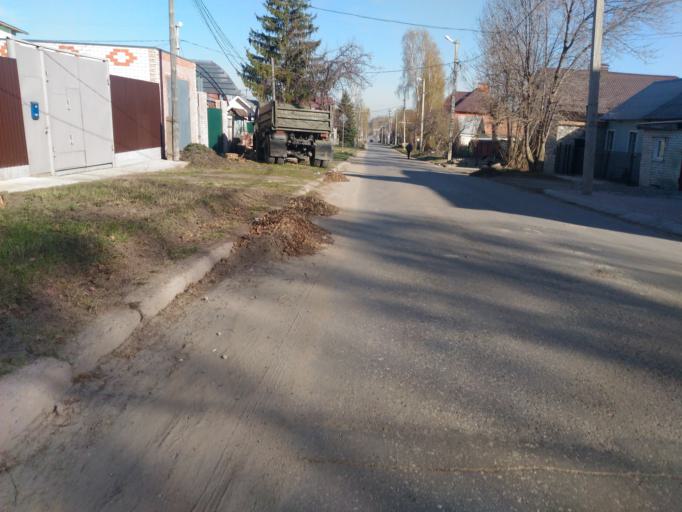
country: RU
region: Ulyanovsk
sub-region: Ulyanovskiy Rayon
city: Ulyanovsk
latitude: 54.3501
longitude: 48.3771
